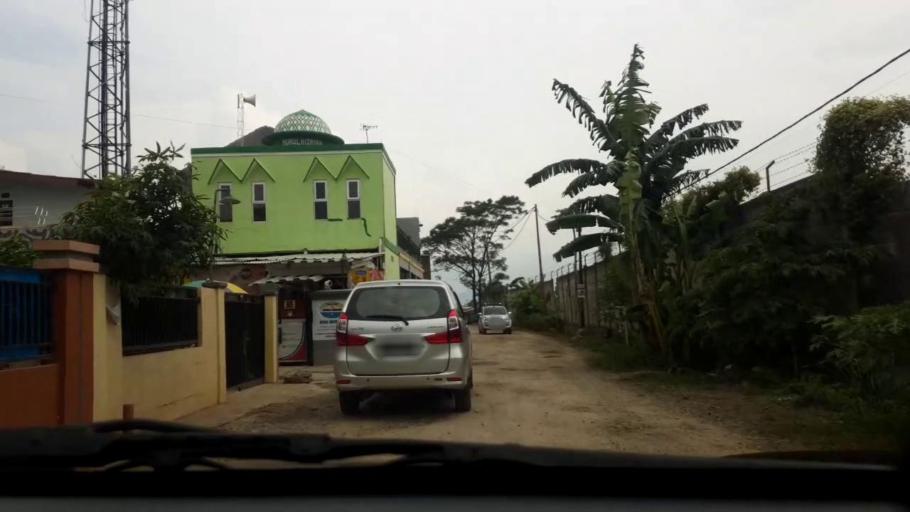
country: ID
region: West Java
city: Cileunyi
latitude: -6.9581
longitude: 107.7159
